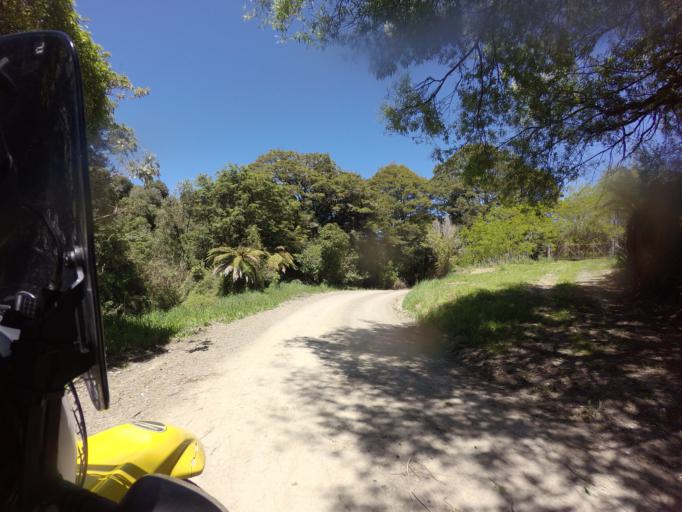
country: NZ
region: Bay of Plenty
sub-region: Opotiki District
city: Opotiki
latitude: -38.4112
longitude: 177.4124
